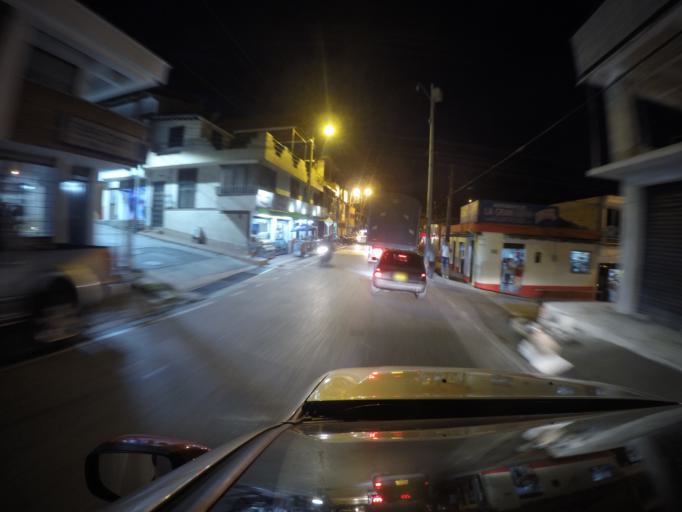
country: CO
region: Tolima
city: Fresno
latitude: 5.1521
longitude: -75.0346
